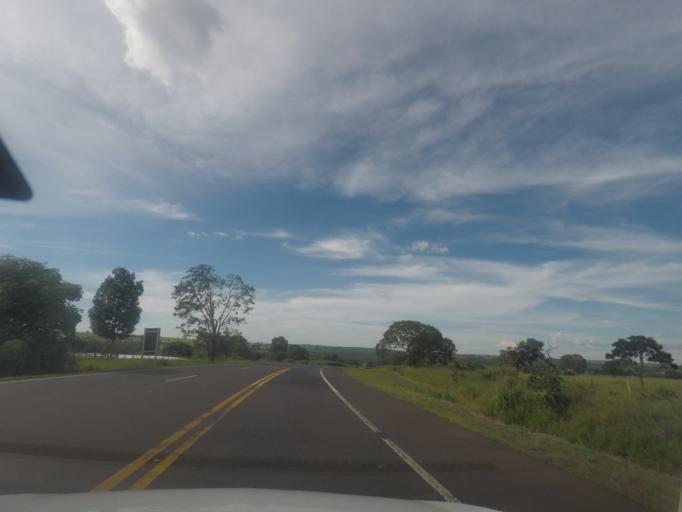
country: BR
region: Minas Gerais
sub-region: Monte Alegre De Minas
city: Monte Alegre de Minas
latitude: -18.9576
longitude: -49.0289
